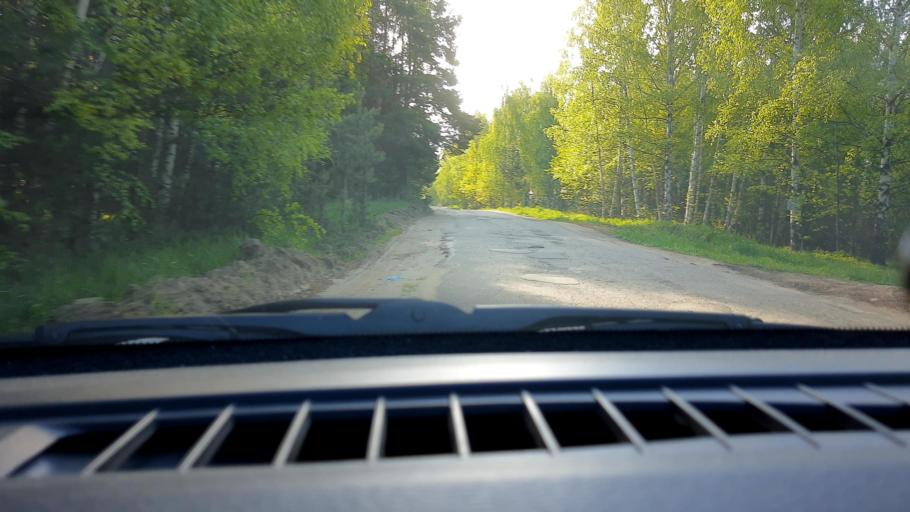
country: RU
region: Nizjnij Novgorod
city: Sitniki
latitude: 56.4144
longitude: 44.0529
